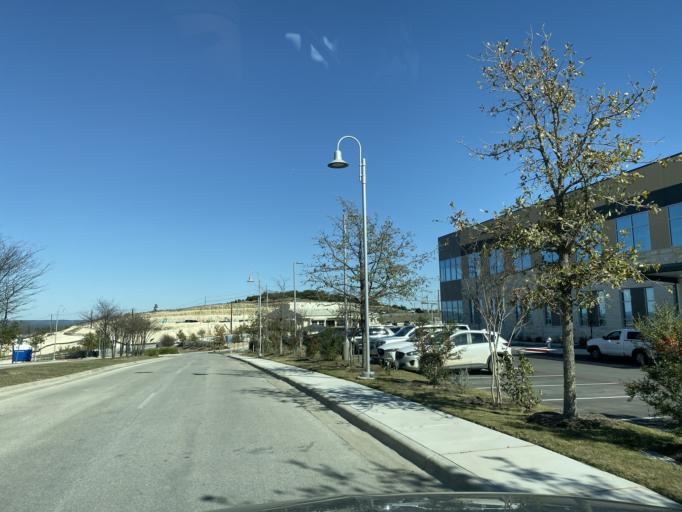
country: US
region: Texas
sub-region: Travis County
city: The Hills
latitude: 30.3327
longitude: -97.9708
